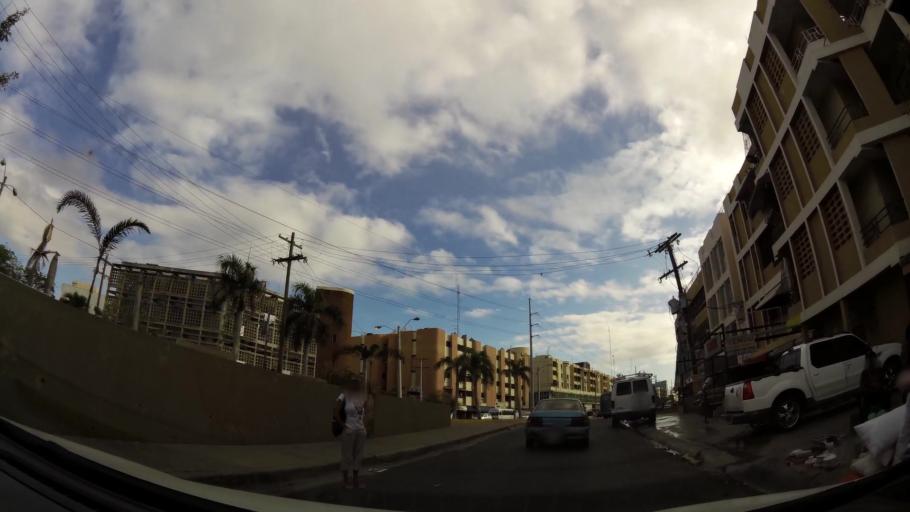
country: DO
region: Nacional
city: San Carlos
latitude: 18.4769
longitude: -69.8921
